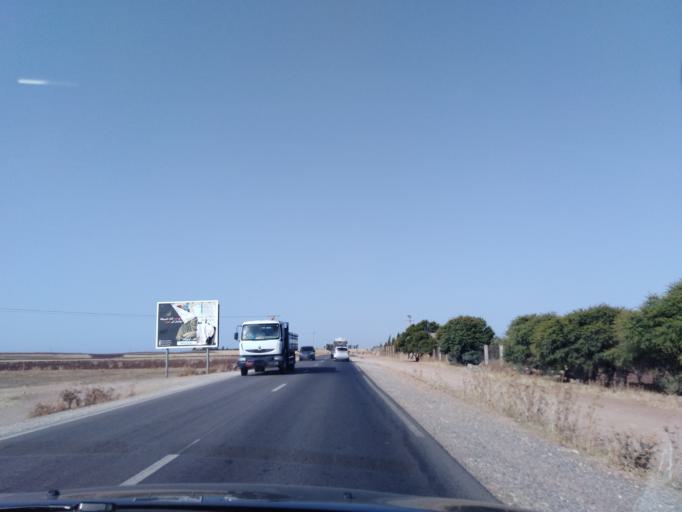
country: MA
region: Doukkala-Abda
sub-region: Safi
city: Safi
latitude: 32.2675
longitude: -8.9469
